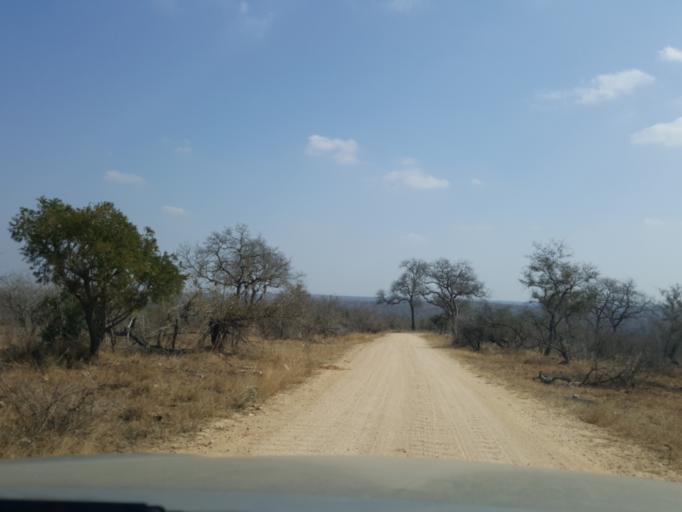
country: ZA
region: Mpumalanga
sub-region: Ehlanzeni District
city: Komatipoort
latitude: -25.2728
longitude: 31.7877
